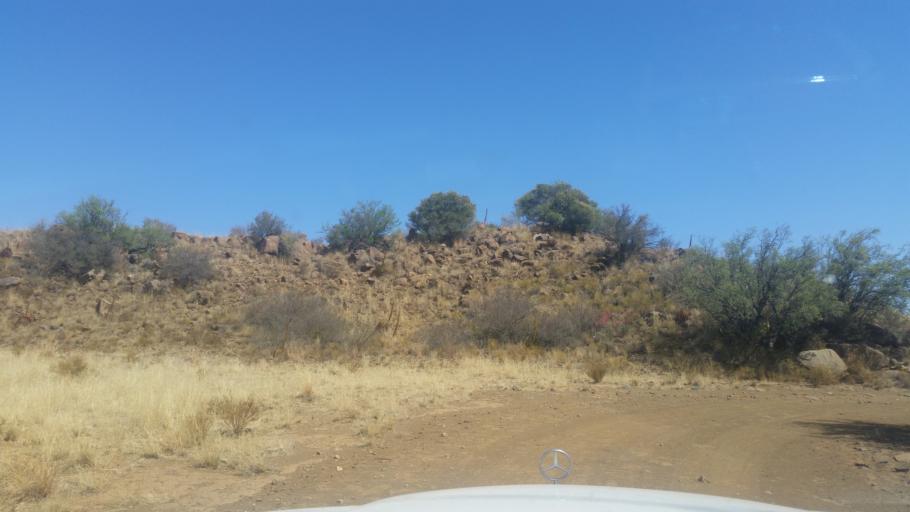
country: ZA
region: Eastern Cape
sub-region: Joe Gqabi District Municipality
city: Burgersdorp
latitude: -30.6927
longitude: 25.7762
